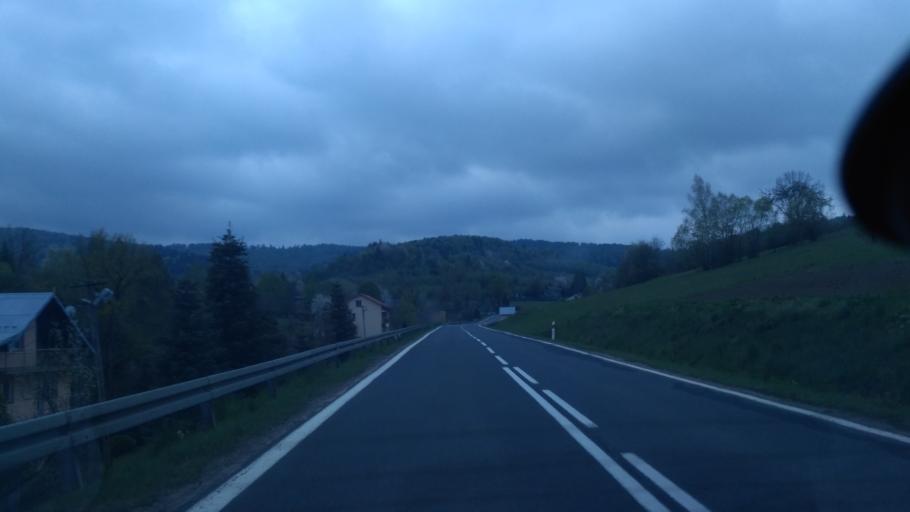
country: PL
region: Subcarpathian Voivodeship
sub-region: Powiat sanocki
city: Tyrawa Woloska
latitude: 49.5720
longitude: 22.3580
